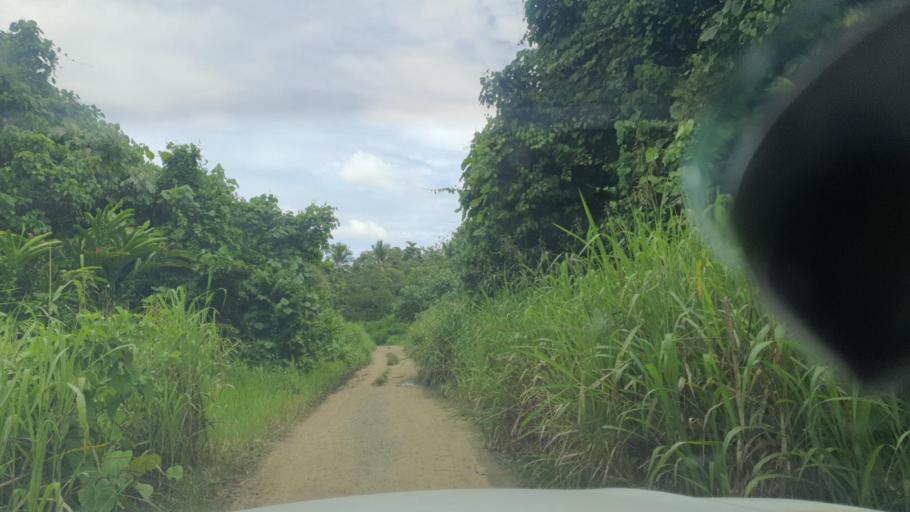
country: SB
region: Guadalcanal
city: Honiara
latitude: -9.4971
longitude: 160.3356
